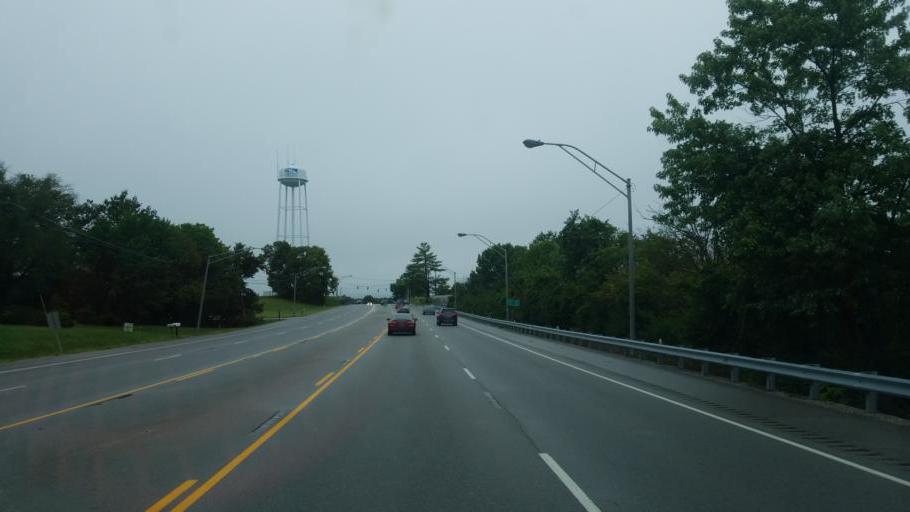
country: US
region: Ohio
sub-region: Brown County
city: Aberdeen
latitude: 38.6418
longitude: -83.7820
